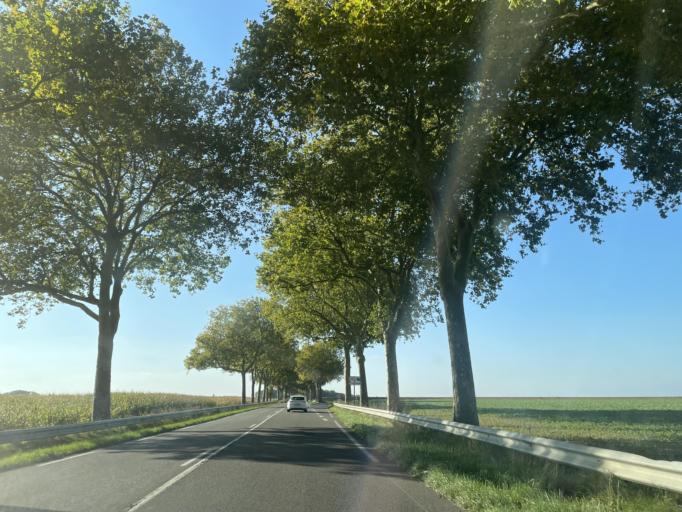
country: FR
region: Ile-de-France
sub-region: Departement de Seine-et-Marne
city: Guerard
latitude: 48.8390
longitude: 2.9704
